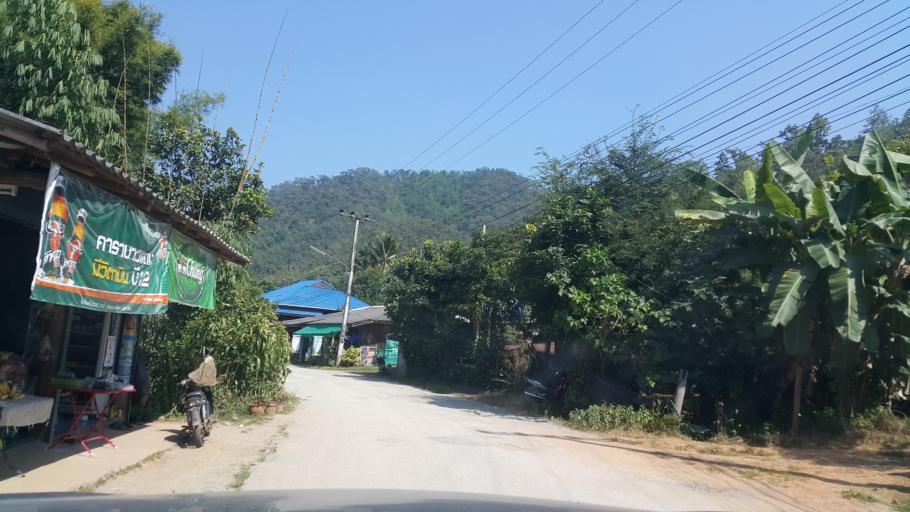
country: TH
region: Chiang Mai
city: Samoeng
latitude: 18.9100
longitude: 98.6032
